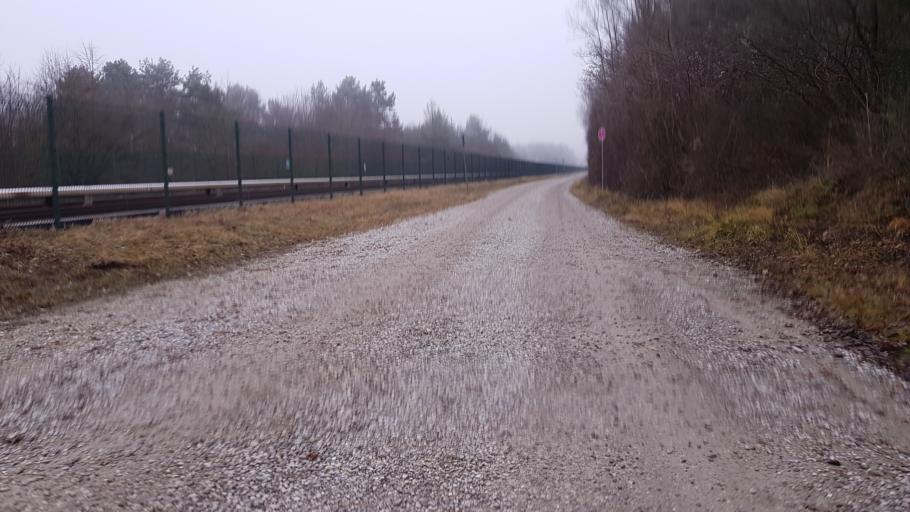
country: DE
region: Bavaria
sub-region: Upper Bavaria
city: Garching bei Munchen
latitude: 48.2259
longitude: 11.6219
